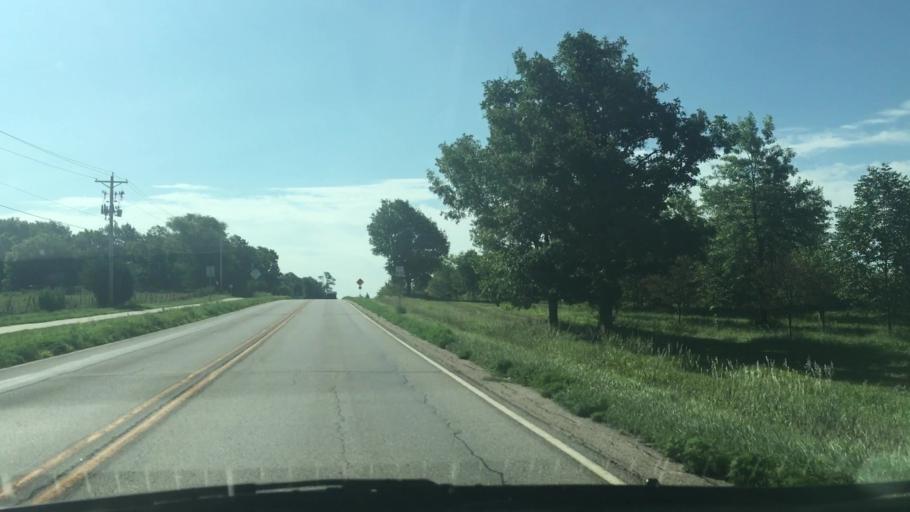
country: US
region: Iowa
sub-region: Johnson County
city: North Liberty
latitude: 41.7324
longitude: -91.5650
